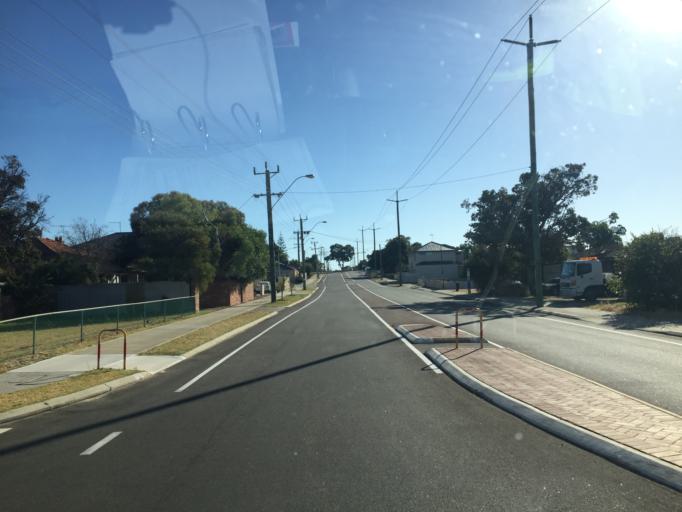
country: AU
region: Western Australia
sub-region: Belmont
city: Rivervale
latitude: -31.9662
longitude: 115.9223
